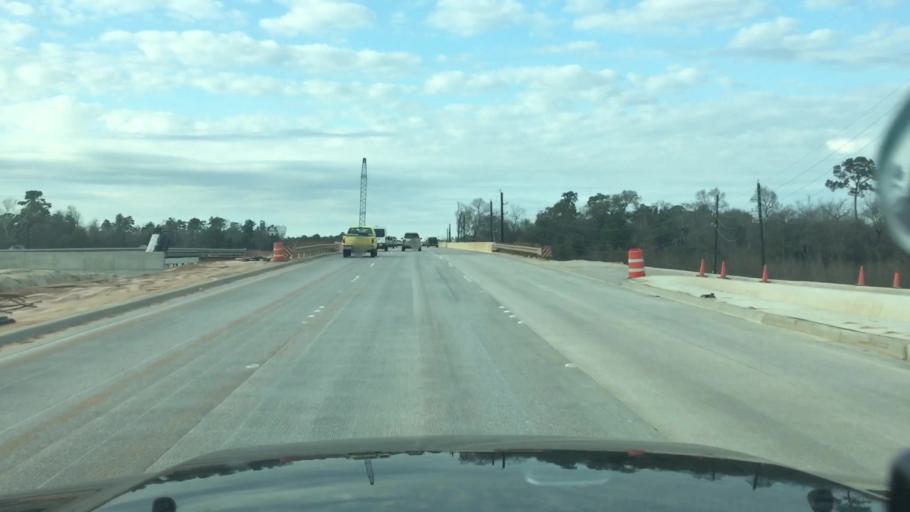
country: US
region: Texas
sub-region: Harris County
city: Tomball
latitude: 30.1167
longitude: -95.6437
